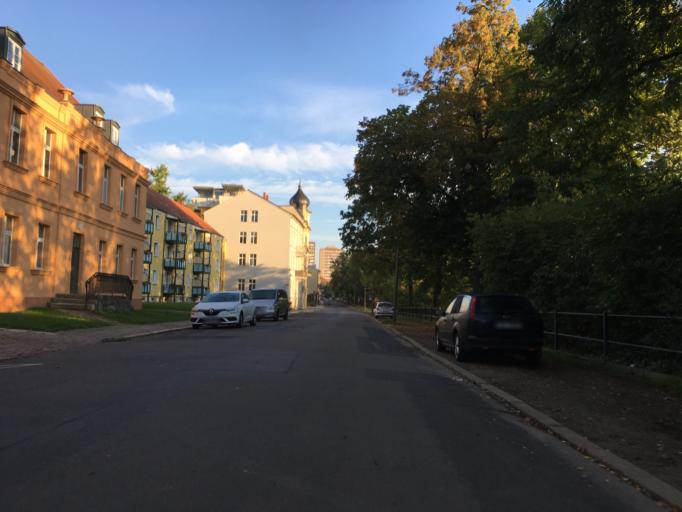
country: DE
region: Brandenburg
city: Frankfurt (Oder)
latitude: 52.3459
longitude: 14.5475
